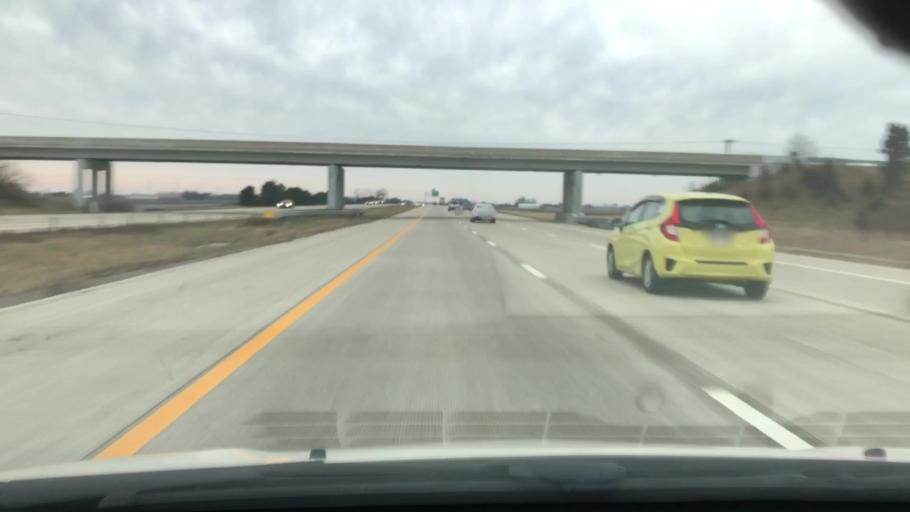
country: US
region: Ohio
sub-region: Wood County
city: Perrysburg
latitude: 41.4920
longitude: -83.6221
